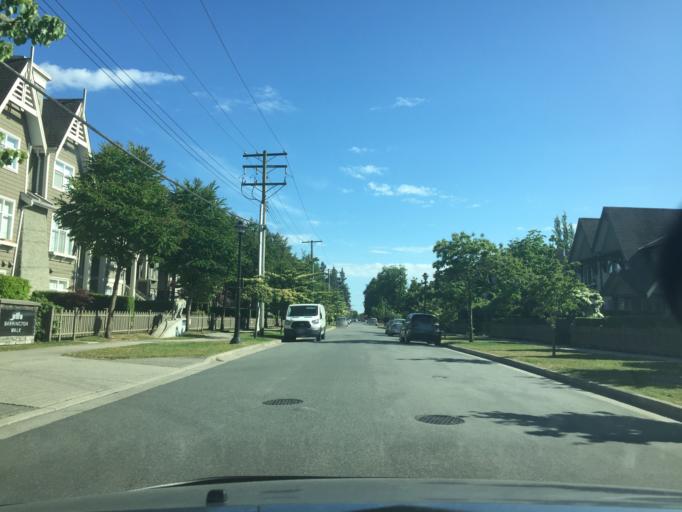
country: CA
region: British Columbia
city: Richmond
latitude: 49.1613
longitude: -123.1226
